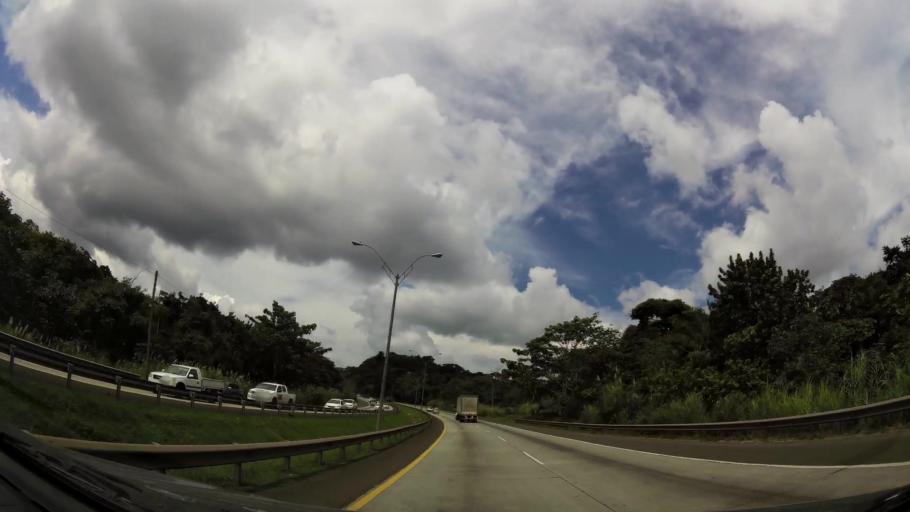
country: PA
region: Panama
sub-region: Distrito Arraijan
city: Arraijan
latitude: 8.9903
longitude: -79.6482
